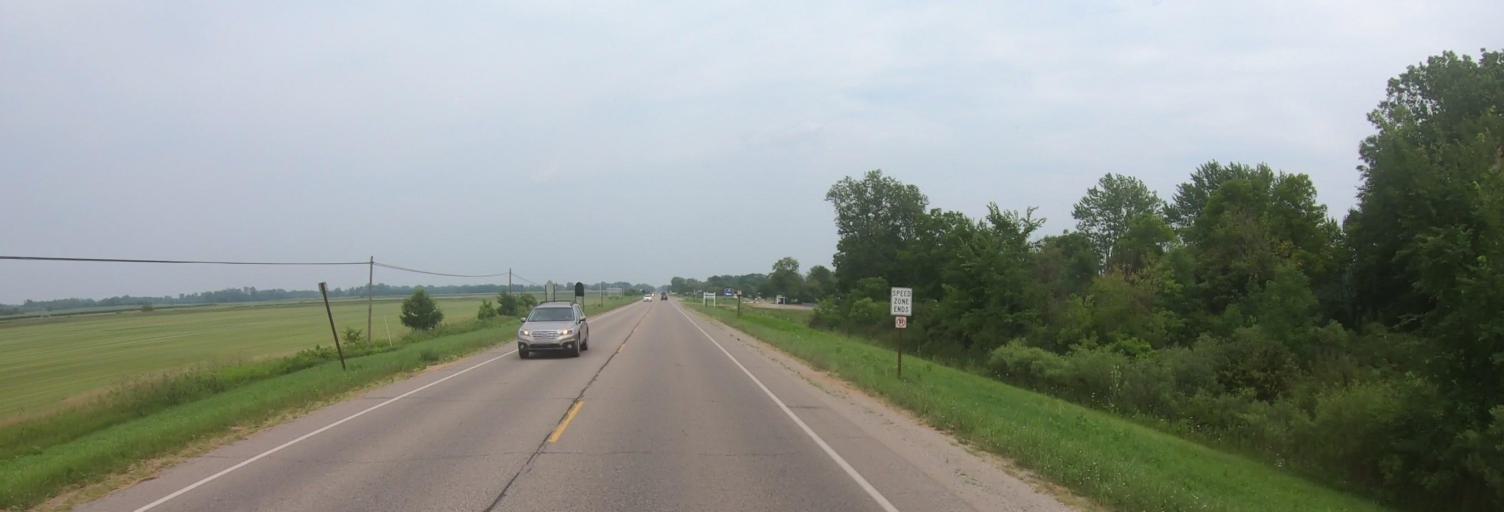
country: US
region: Michigan
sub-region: Shiawassee County
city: Durand
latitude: 42.9257
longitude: -83.9828
